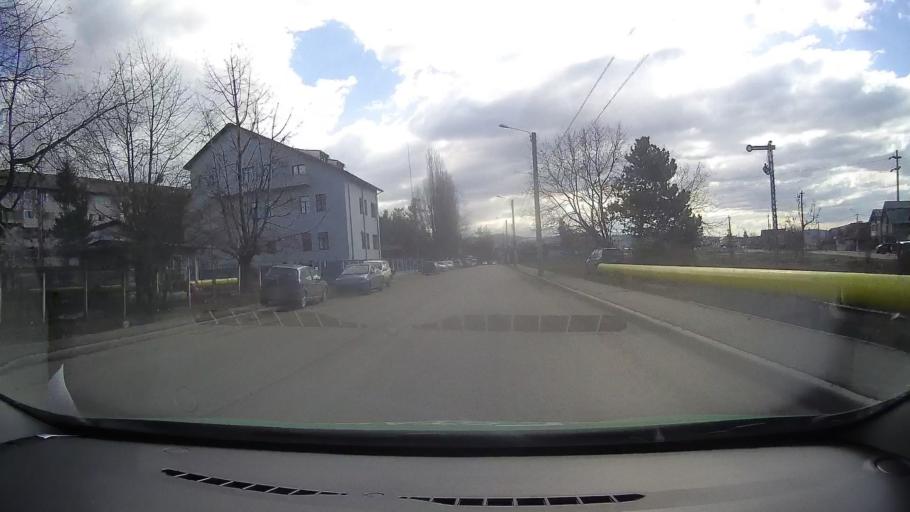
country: RO
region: Dambovita
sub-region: Oras Pucioasa
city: Pucioasa
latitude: 45.0774
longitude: 25.4300
